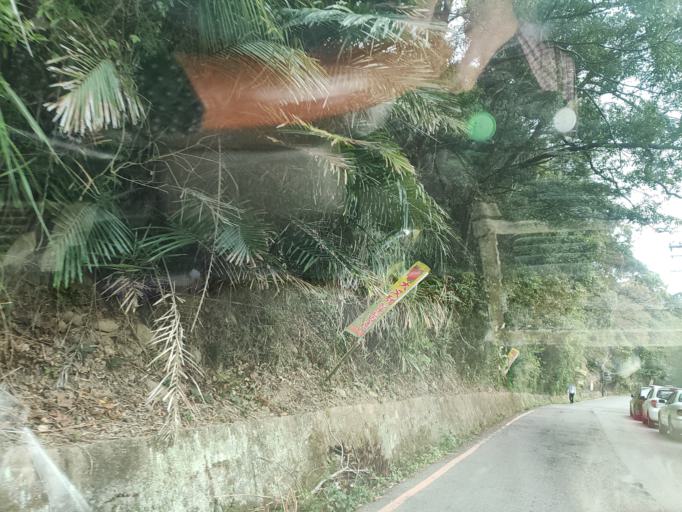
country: TW
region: Taiwan
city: Fengyuan
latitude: 24.3577
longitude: 120.7738
